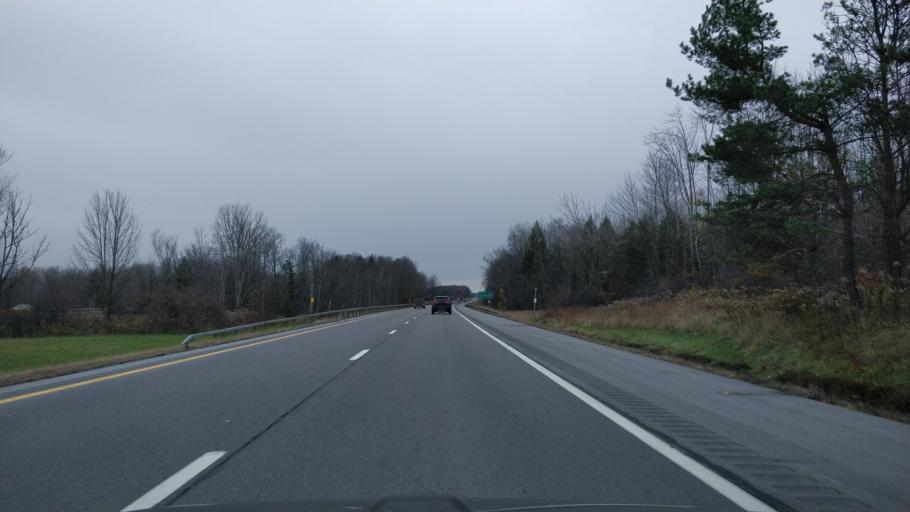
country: US
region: New York
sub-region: Oswego County
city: Pulaski
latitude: 43.5463
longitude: -76.1150
